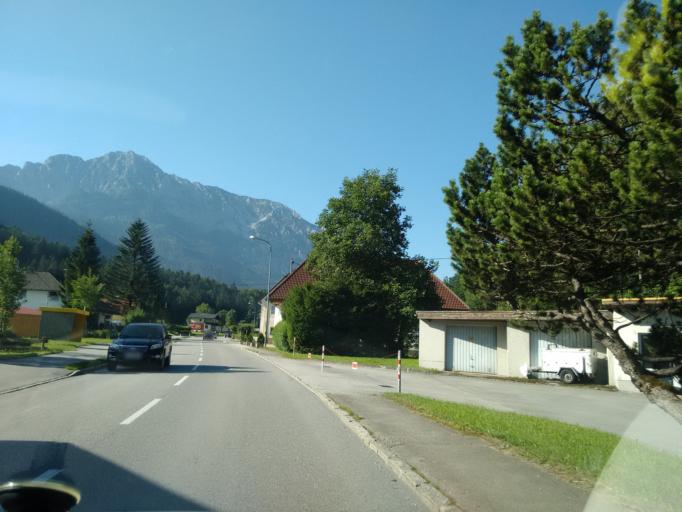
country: AT
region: Styria
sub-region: Politischer Bezirk Liezen
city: Ardning
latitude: 47.6592
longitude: 14.3385
